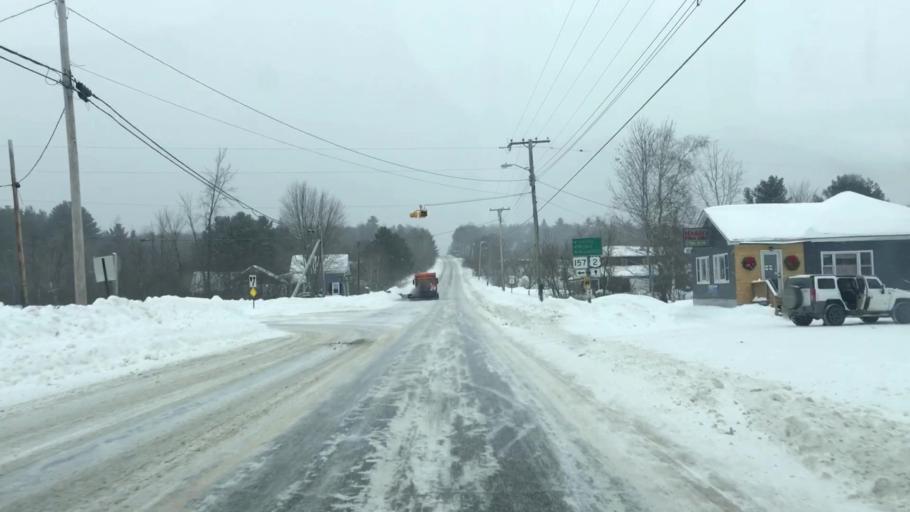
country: US
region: Maine
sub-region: Penobscot County
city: Medway
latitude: 45.5209
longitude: -68.3523
